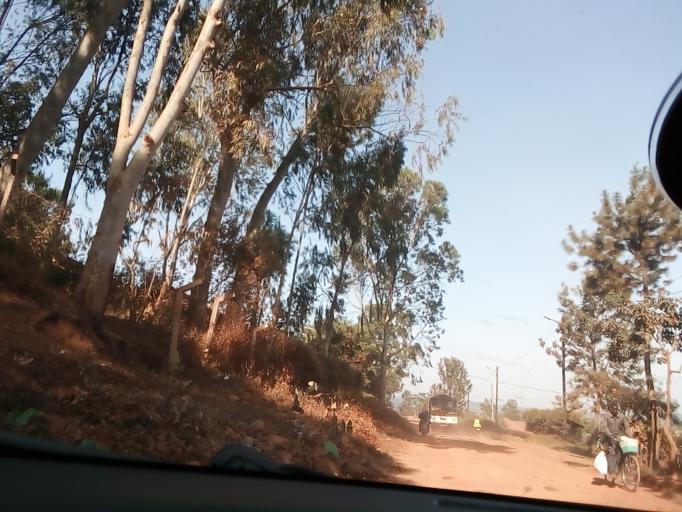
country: UG
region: Central Region
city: Masaka
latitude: -0.3349
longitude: 31.7332
